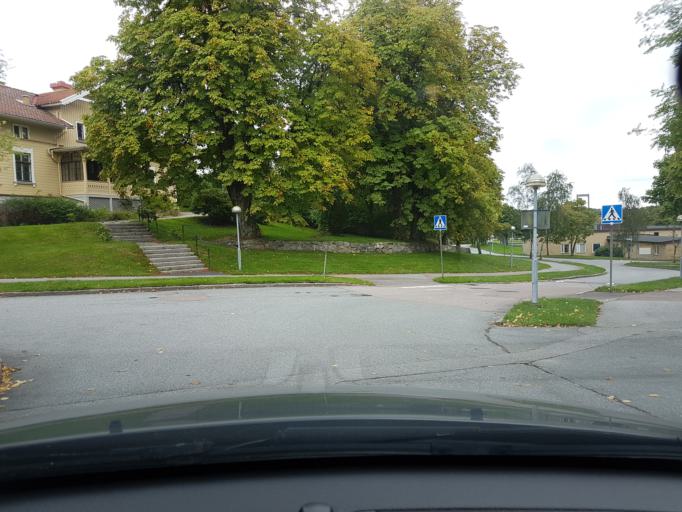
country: SE
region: Vaestra Goetaland
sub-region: Goteborg
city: Majorna
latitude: 57.7083
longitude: 11.8982
